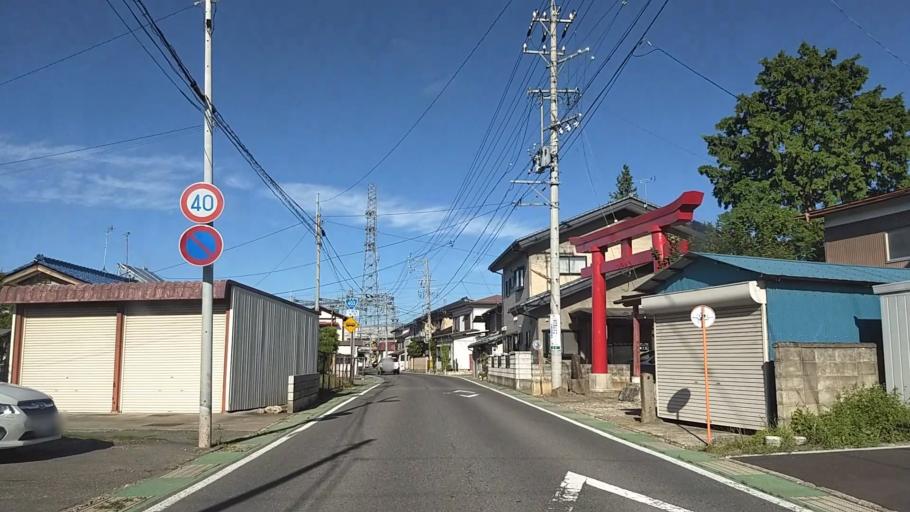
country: JP
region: Nagano
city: Nagano-shi
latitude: 36.5405
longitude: 138.1288
